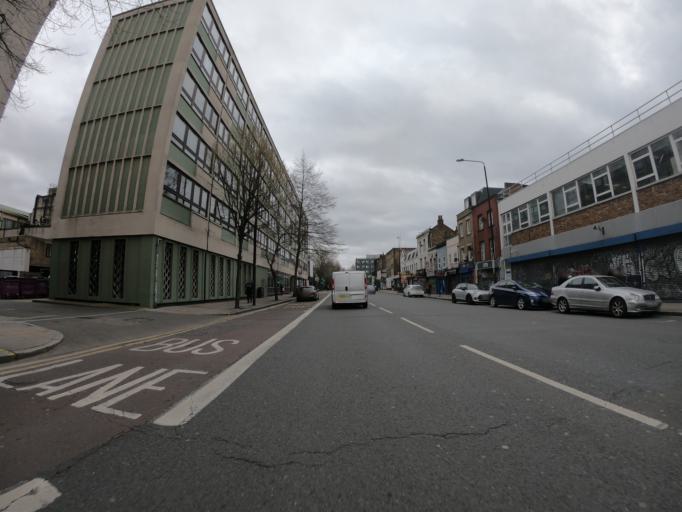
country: GB
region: England
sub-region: Greater London
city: Bethnal Green
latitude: 51.5303
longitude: -0.0561
